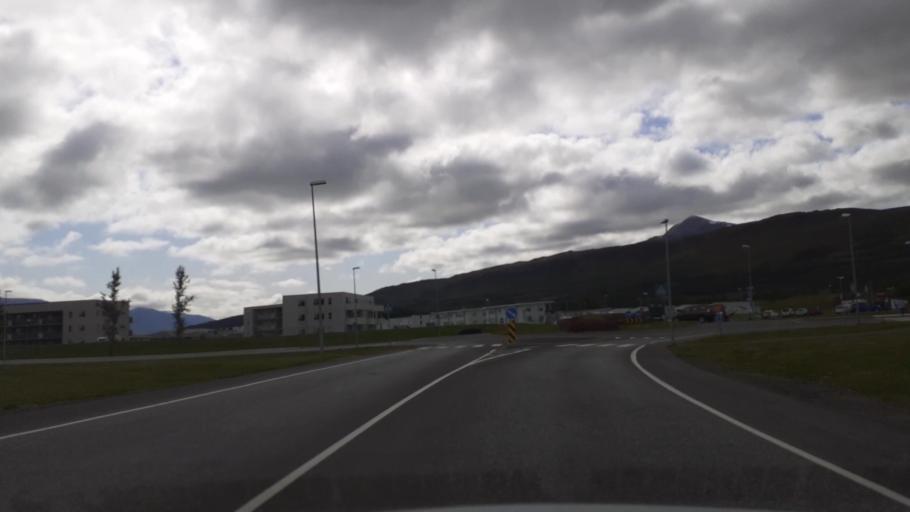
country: IS
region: Northeast
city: Akureyri
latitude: 65.6702
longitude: -18.1074
